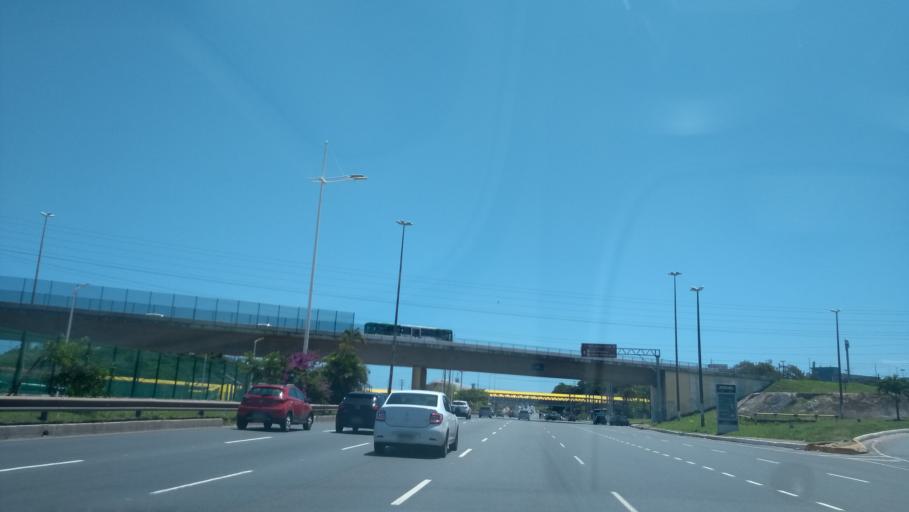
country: BR
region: Bahia
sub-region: Salvador
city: Salvador
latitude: -12.9420
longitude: -38.4193
